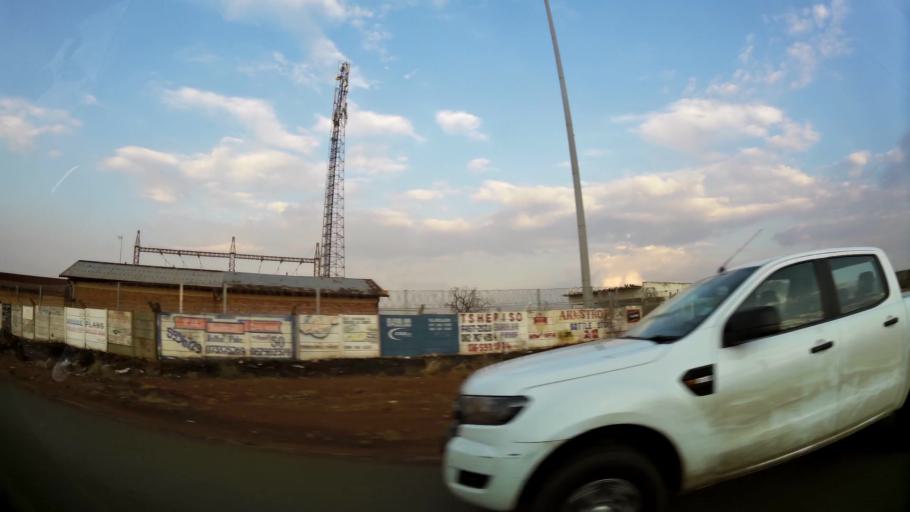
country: ZA
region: Gauteng
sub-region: City of Johannesburg Metropolitan Municipality
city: Orange Farm
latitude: -26.5600
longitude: 27.8610
